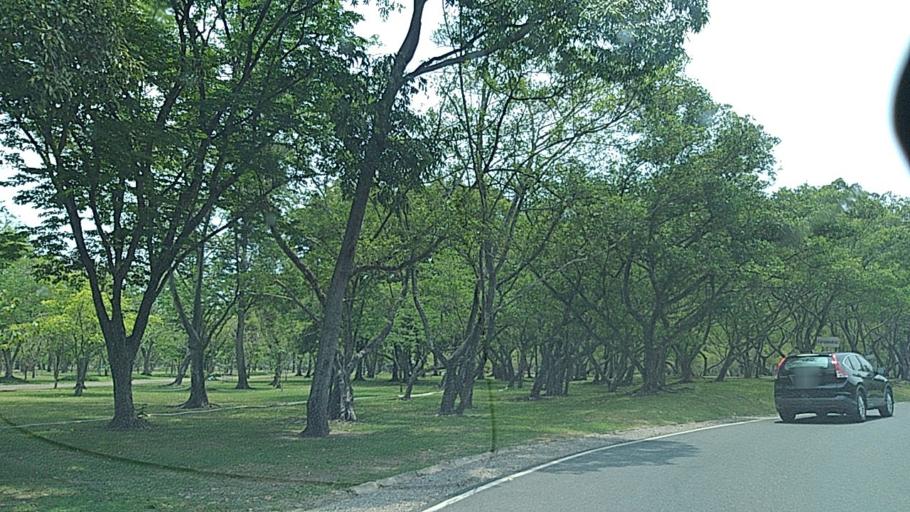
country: TH
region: Bangkok
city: Thawi Watthana
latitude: 13.7746
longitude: 100.3221
